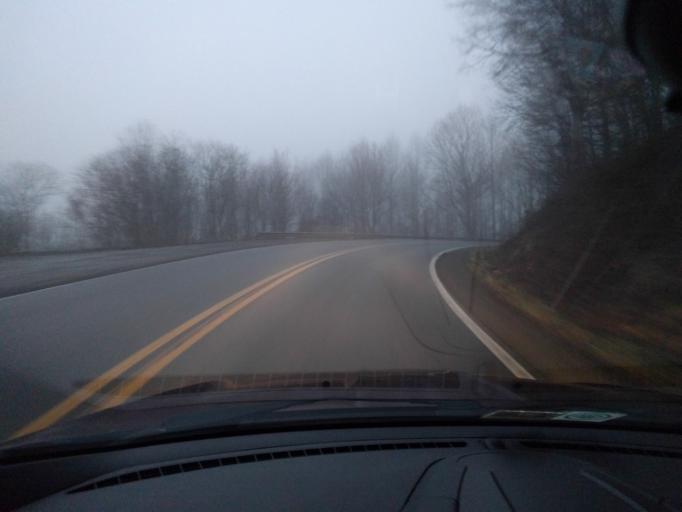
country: US
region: West Virginia
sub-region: Greenbrier County
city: Rainelle
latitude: 37.9733
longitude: -80.8192
